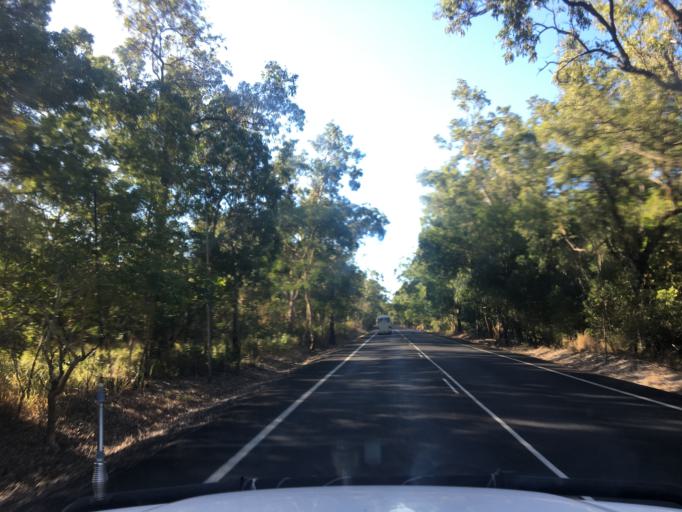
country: AU
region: Queensland
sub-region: Cairns
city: Palm Cove
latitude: -16.6725
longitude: 145.5680
